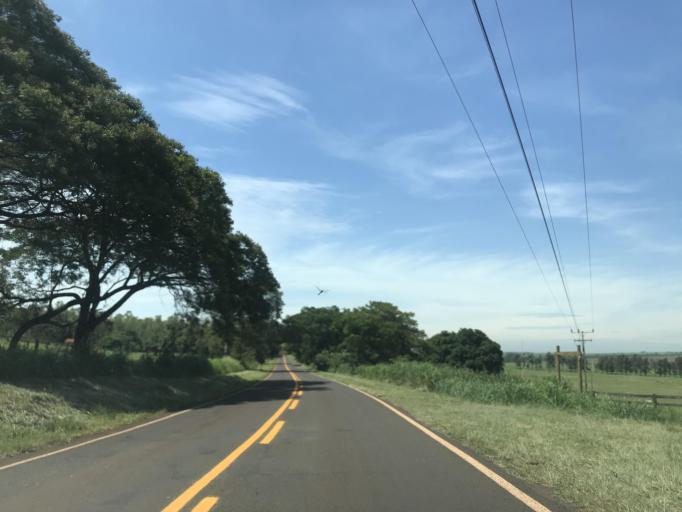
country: BR
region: Parana
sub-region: Terra Rica
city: Terra Rica
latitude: -22.7827
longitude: -52.6573
